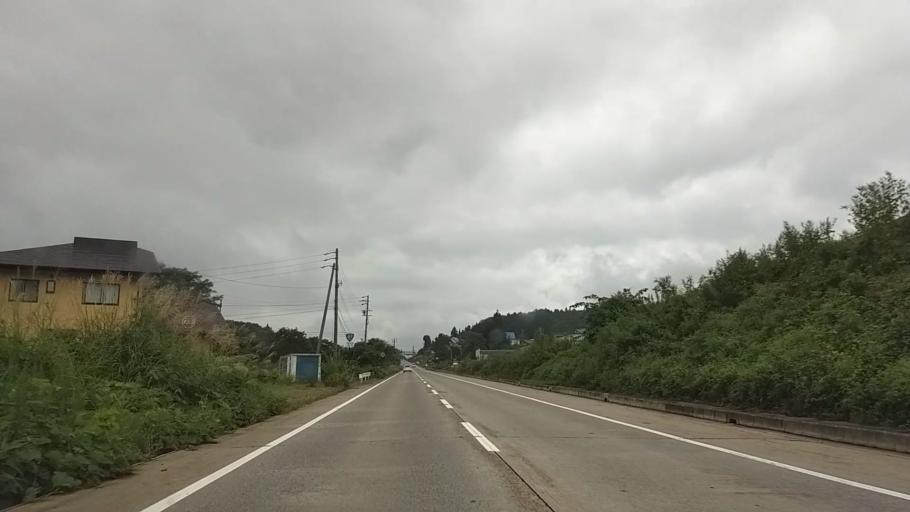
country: JP
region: Nagano
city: Iiyama
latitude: 36.8091
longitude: 138.3344
